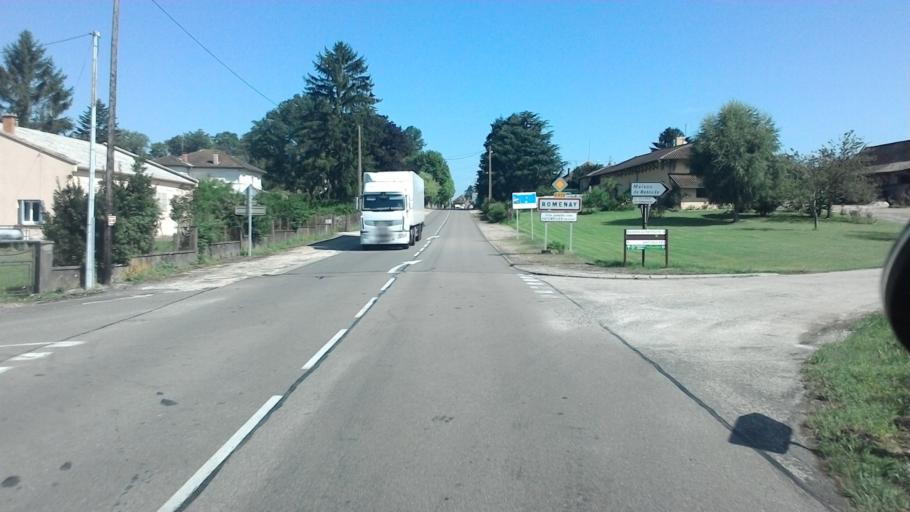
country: FR
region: Bourgogne
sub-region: Departement de Saone-et-Loire
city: Romenay
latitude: 46.4988
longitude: 5.0677
